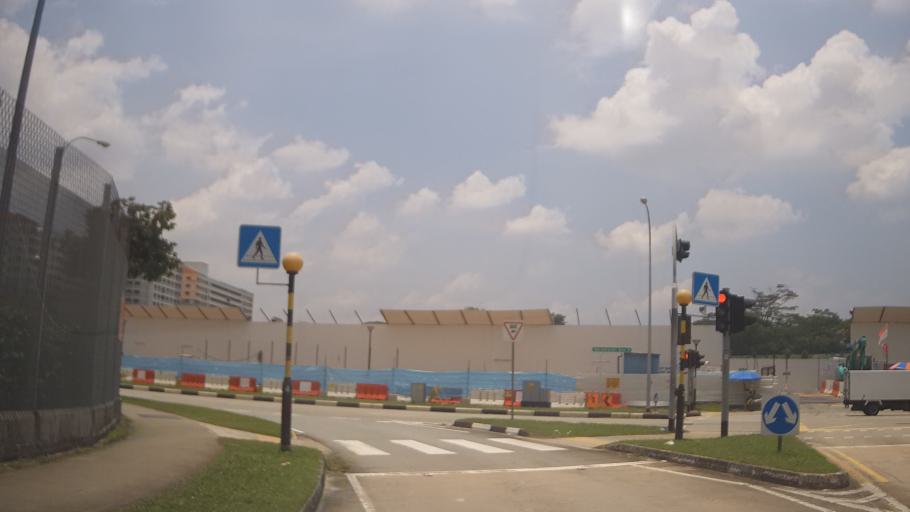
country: MY
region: Johor
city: Johor Bahru
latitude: 1.4474
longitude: 103.7923
